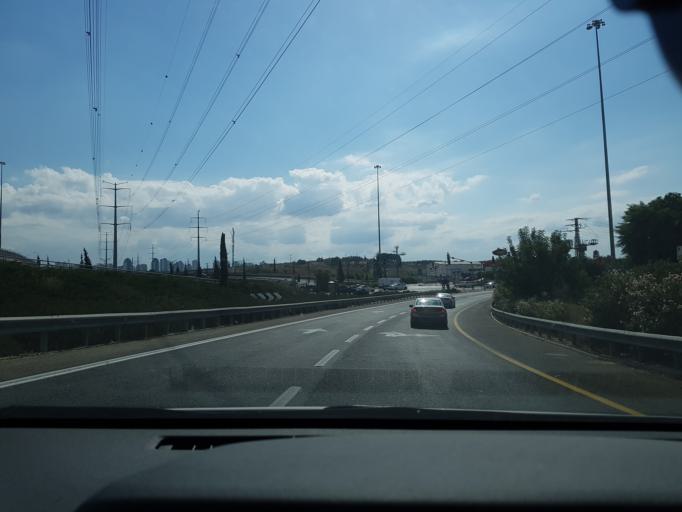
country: IL
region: Central District
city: Ness Ziona
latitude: 31.9488
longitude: 34.8007
